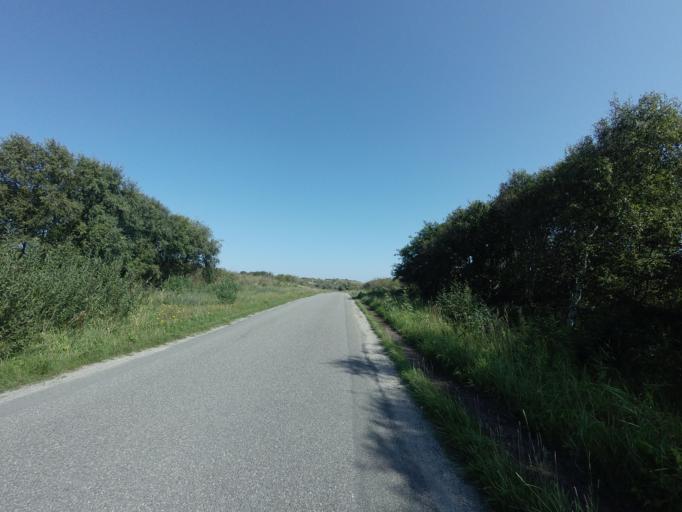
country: NL
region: Friesland
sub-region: Gemeente Schiermonnikoog
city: Schiermonnikoog
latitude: 53.4952
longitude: 6.1856
